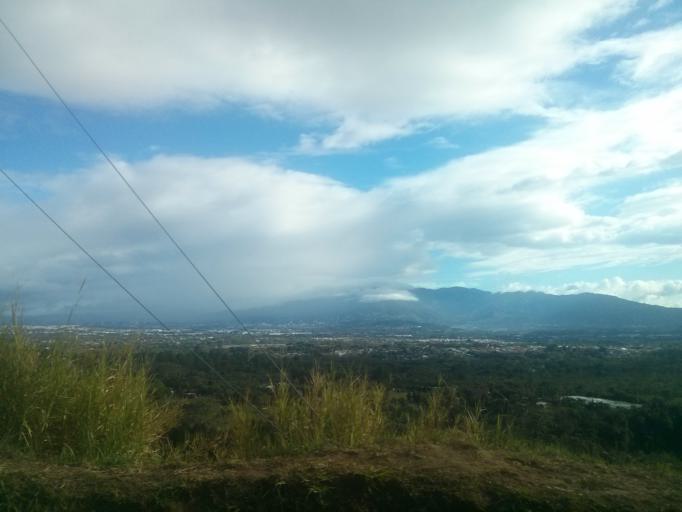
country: CR
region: Alajuela
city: Sabanilla
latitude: 10.0537
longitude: -84.2029
